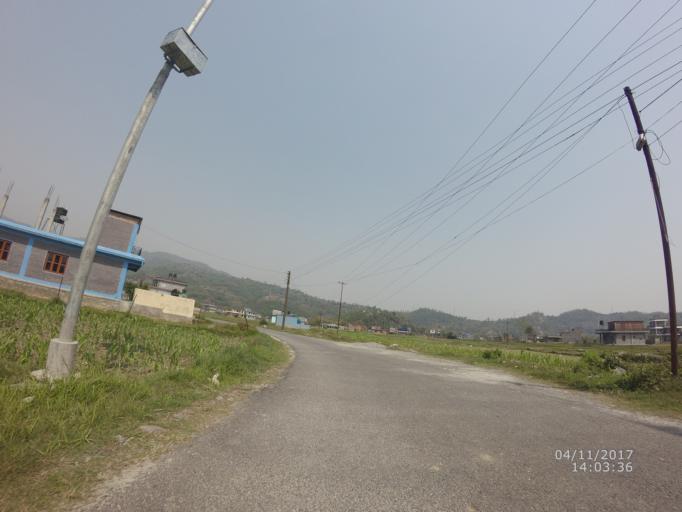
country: NP
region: Western Region
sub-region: Gandaki Zone
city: Pokhara
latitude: 28.1856
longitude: 84.0497
